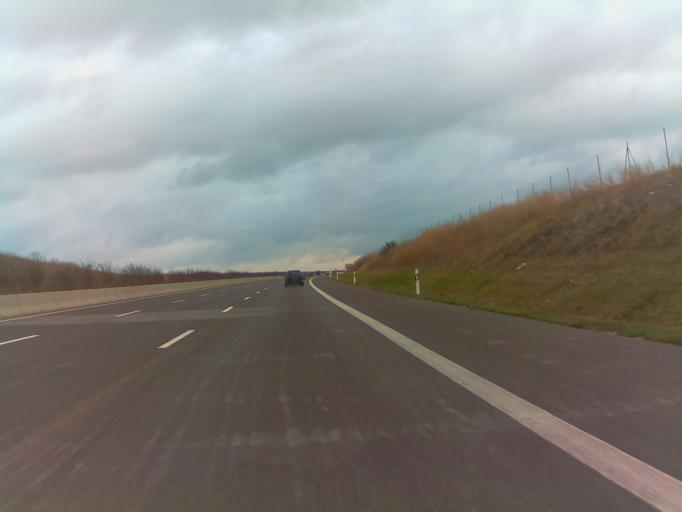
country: DE
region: Thuringia
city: Magdala
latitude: 50.8916
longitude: 11.4619
